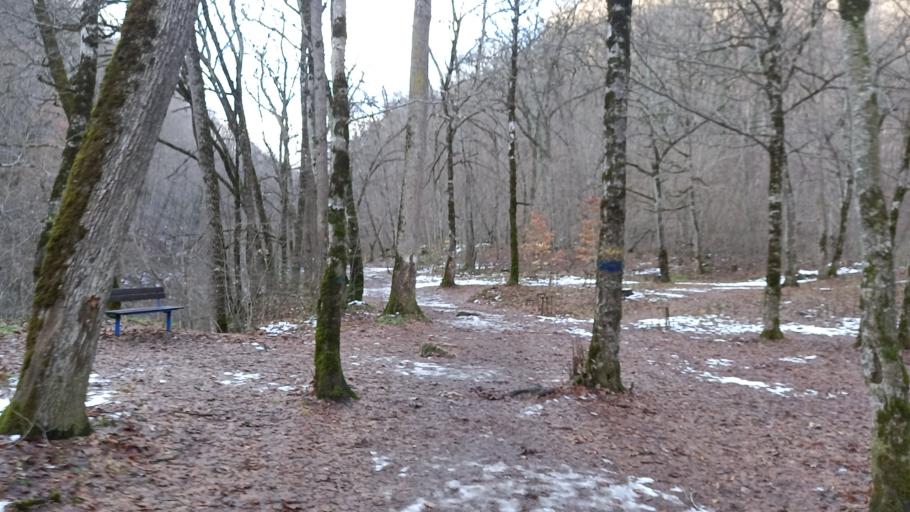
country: RU
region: Adygeya
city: Kamennomostskiy
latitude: 44.2694
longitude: 40.1853
